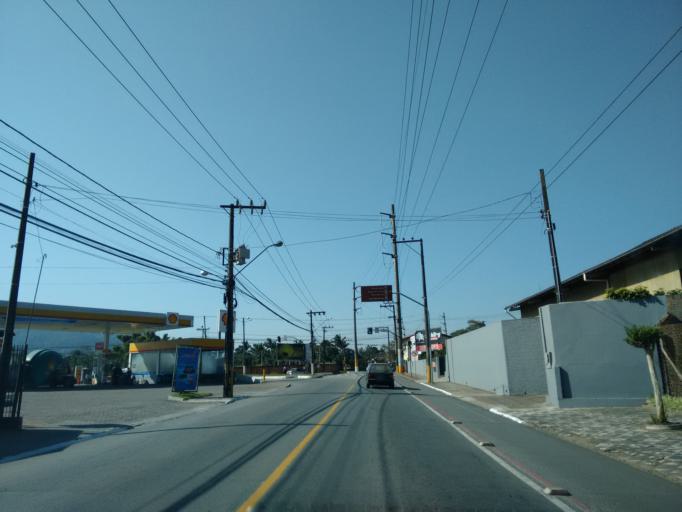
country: BR
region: Santa Catarina
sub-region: Jaragua Do Sul
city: Jaragua do Sul
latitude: -26.4948
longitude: -49.0707
